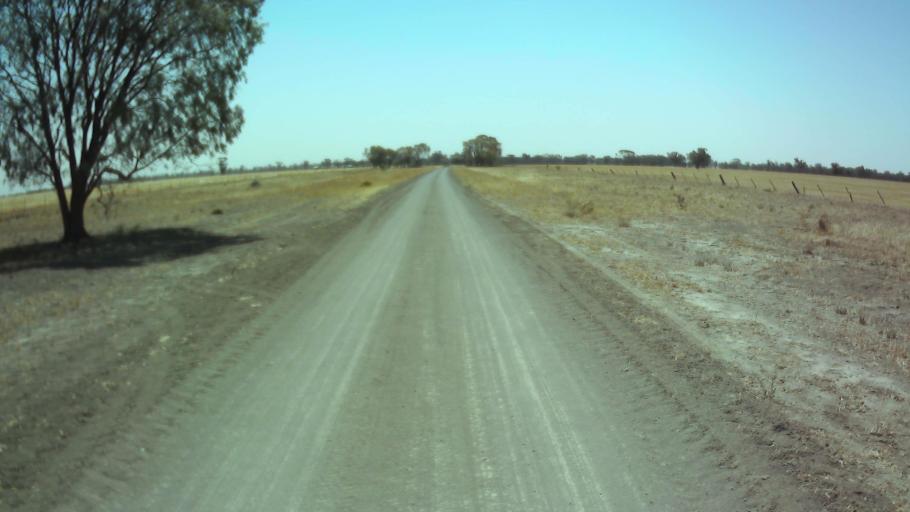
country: AU
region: New South Wales
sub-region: Weddin
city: Grenfell
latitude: -33.9914
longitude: 147.8634
